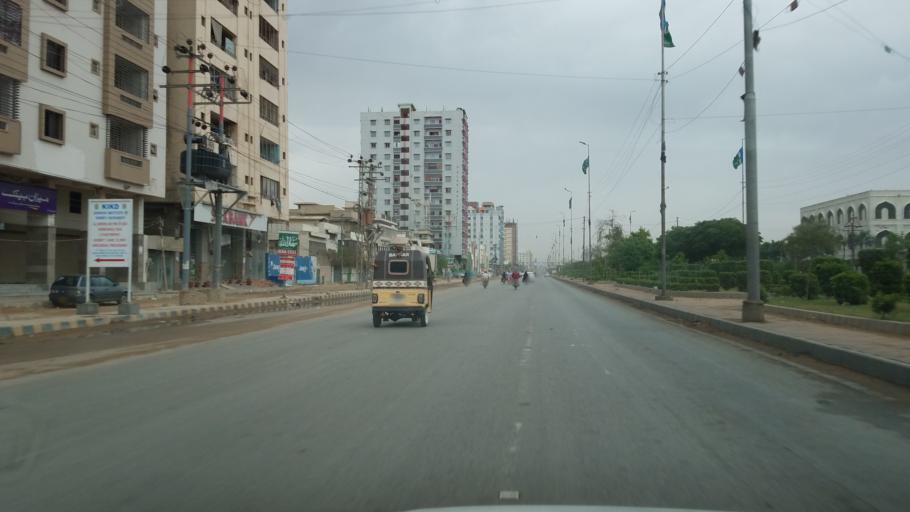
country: PK
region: Sindh
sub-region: Karachi District
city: Karachi
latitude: 24.9225
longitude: 67.0577
